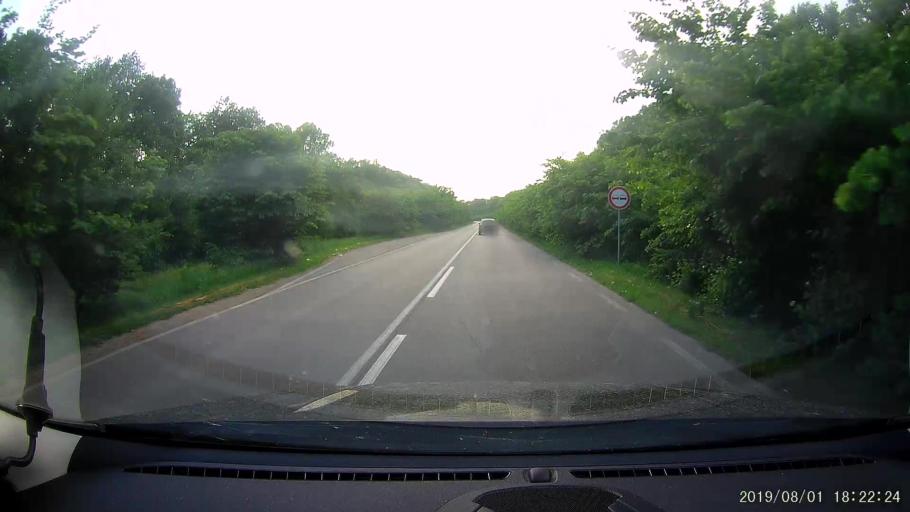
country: BG
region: Shumen
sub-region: Obshtina Kaolinovo
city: Kaolinovo
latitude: 43.6395
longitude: 27.0515
